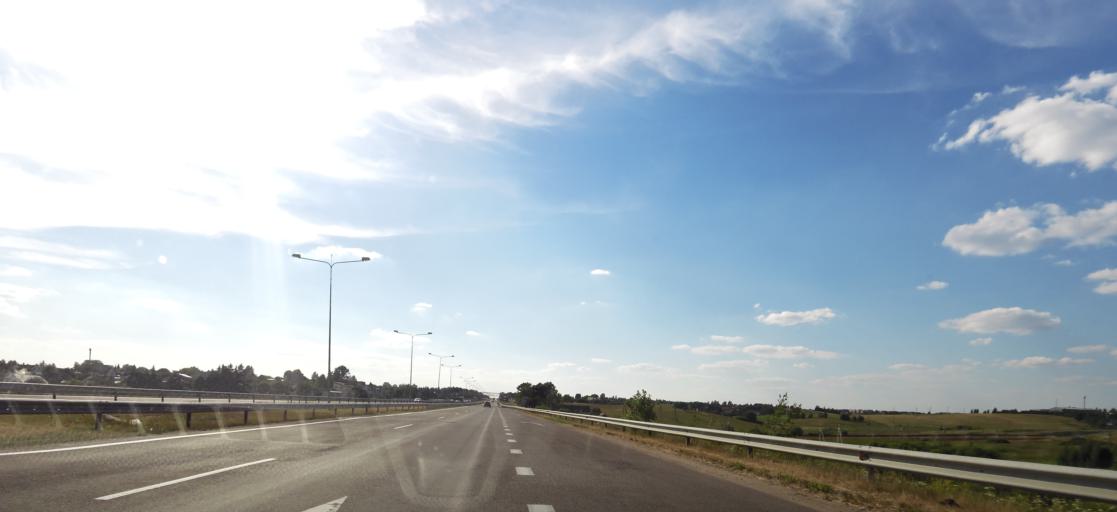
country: LT
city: Skaidiskes
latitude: 54.6381
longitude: 25.3665
